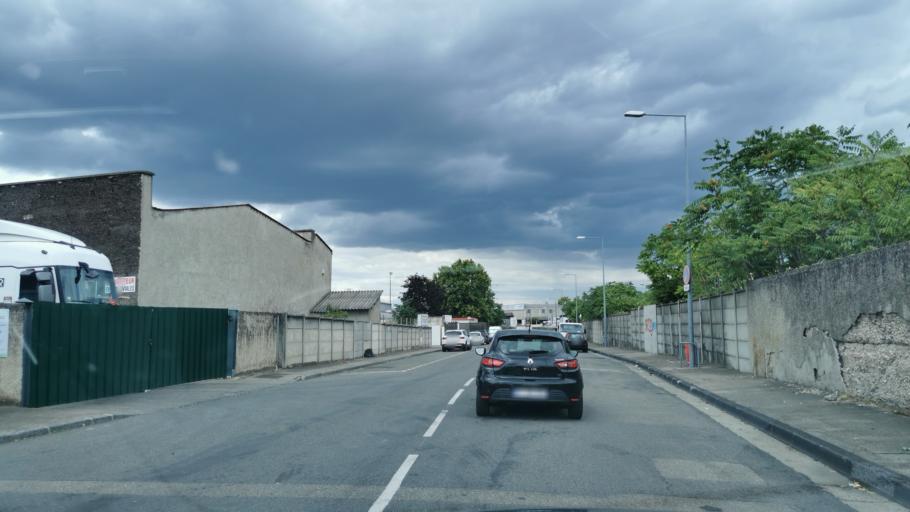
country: FR
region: Rhone-Alpes
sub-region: Departement du Rhone
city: Saint-Fons
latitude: 45.7110
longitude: 4.8494
